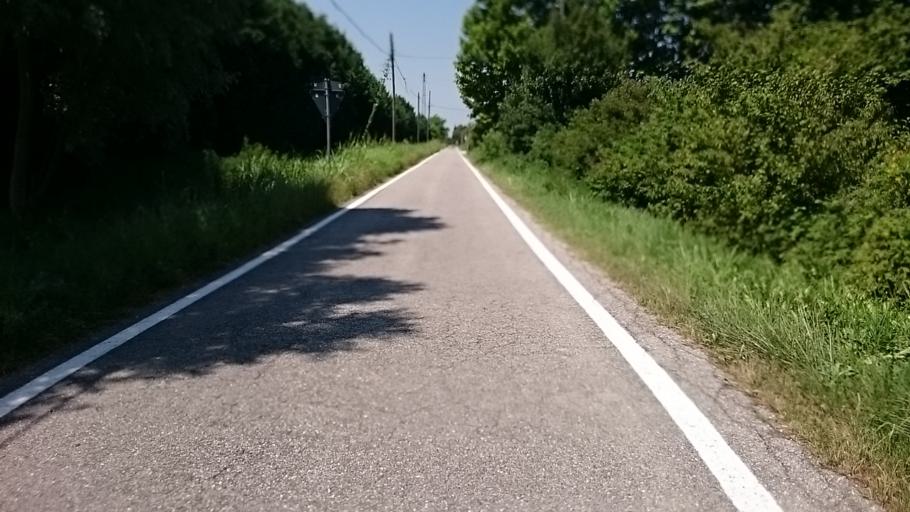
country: IT
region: Veneto
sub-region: Provincia di Venezia
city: Caselle
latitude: 45.5092
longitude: 11.9923
